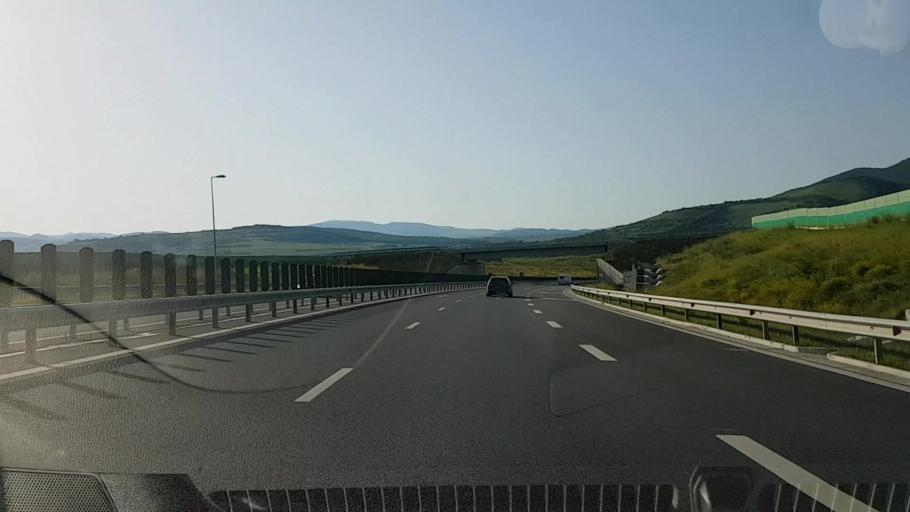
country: RO
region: Alba
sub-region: Comuna Miraslau
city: Miraslau
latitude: 46.3482
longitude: 23.7263
